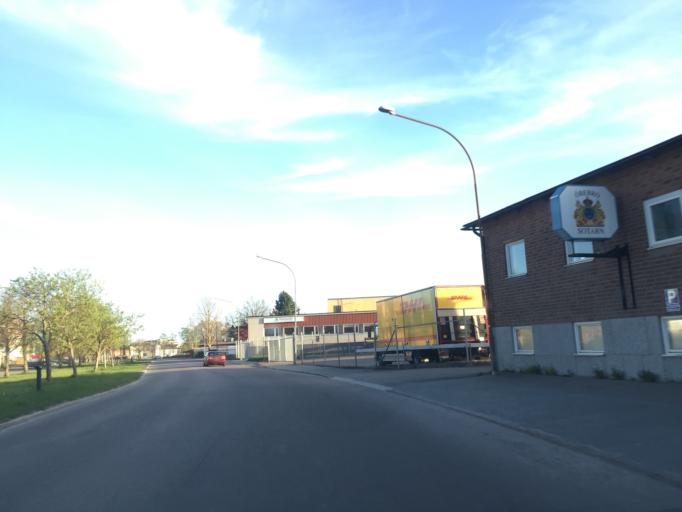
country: SE
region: OErebro
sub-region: Orebro Kommun
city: Orebro
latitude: 59.2901
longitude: 15.2100
